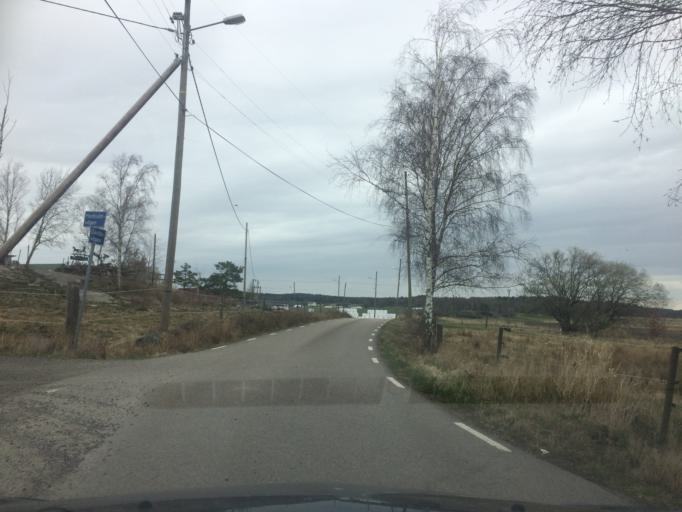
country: SE
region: Vaestra Goetaland
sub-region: Goteborg
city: Majorna
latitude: 57.8034
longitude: 11.8818
